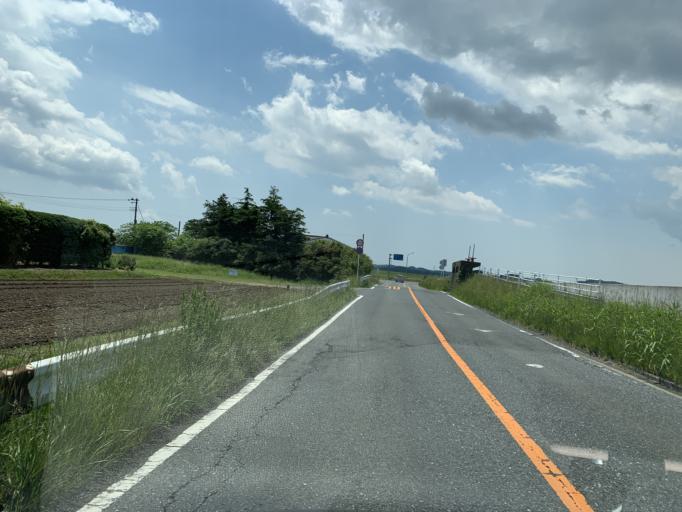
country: JP
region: Miyagi
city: Matsushima
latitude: 38.4494
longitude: 141.0811
